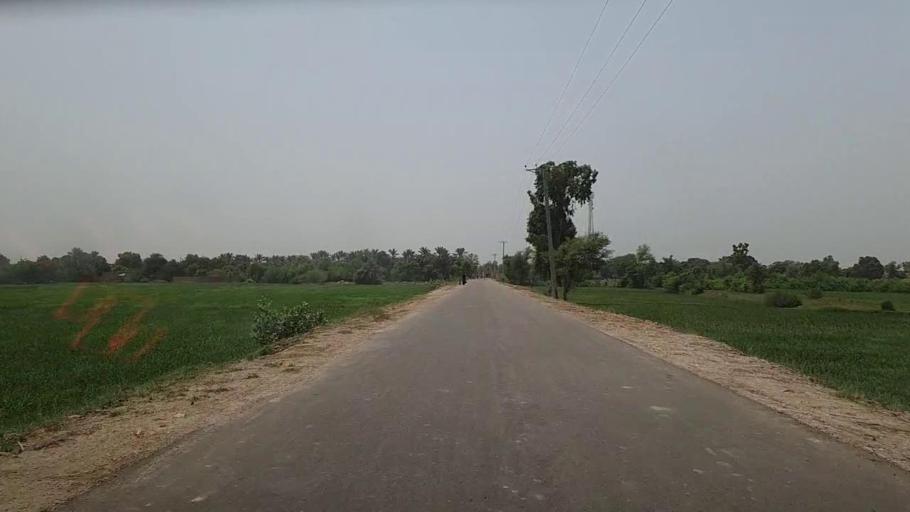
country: PK
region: Sindh
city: Sita Road
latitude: 27.0432
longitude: 67.9003
